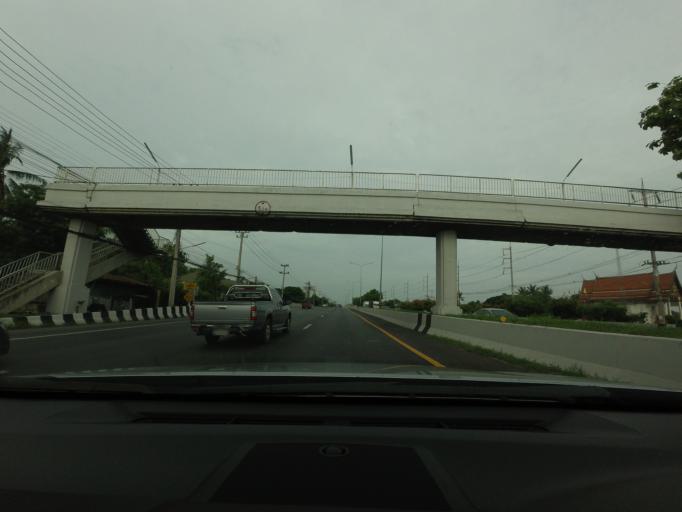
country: TH
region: Phetchaburi
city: Phetchaburi
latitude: 13.1185
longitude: 99.9040
